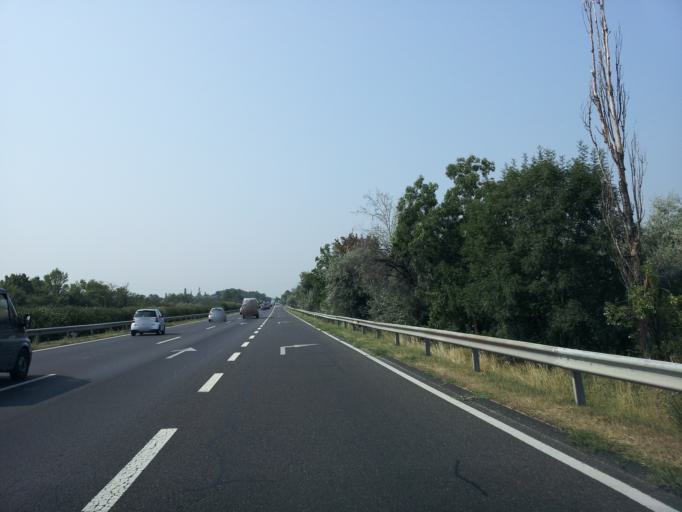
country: HU
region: Fejer
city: Martonvasar
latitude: 47.3349
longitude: 18.7813
